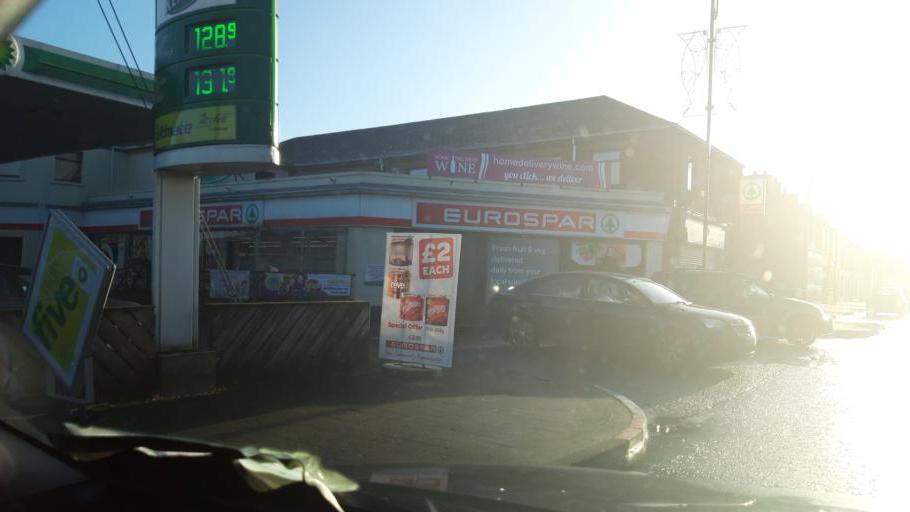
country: GB
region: Northern Ireland
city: Garvagh
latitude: 54.9853
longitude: -6.6866
